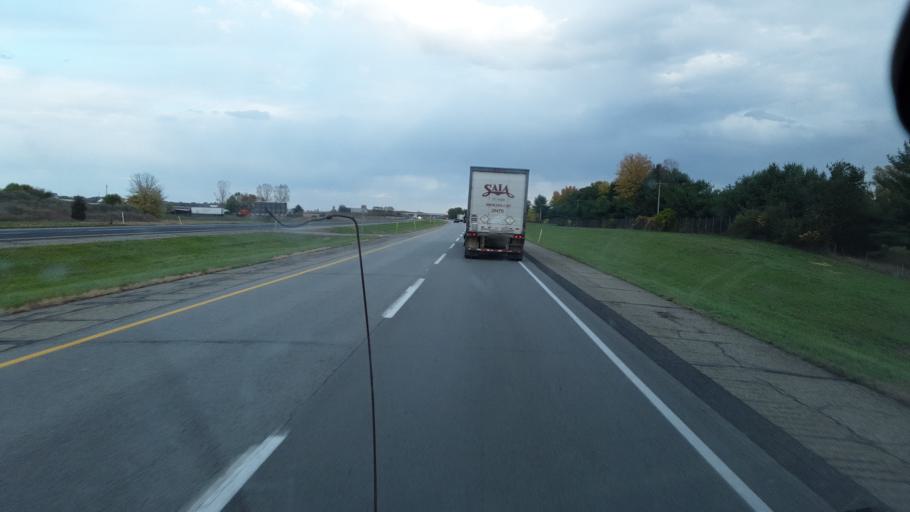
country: US
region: Michigan
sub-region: Saint Joseph County
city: Sturgis
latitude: 41.7482
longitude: -85.3692
